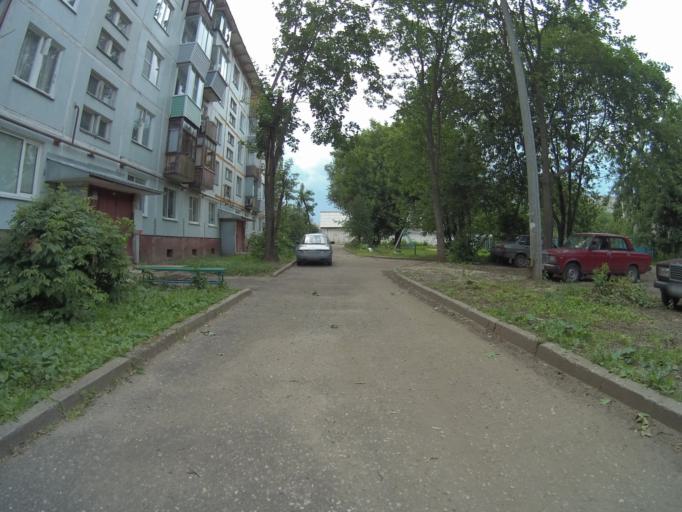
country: RU
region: Vladimir
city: Vladimir
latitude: 56.1354
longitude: 40.3721
